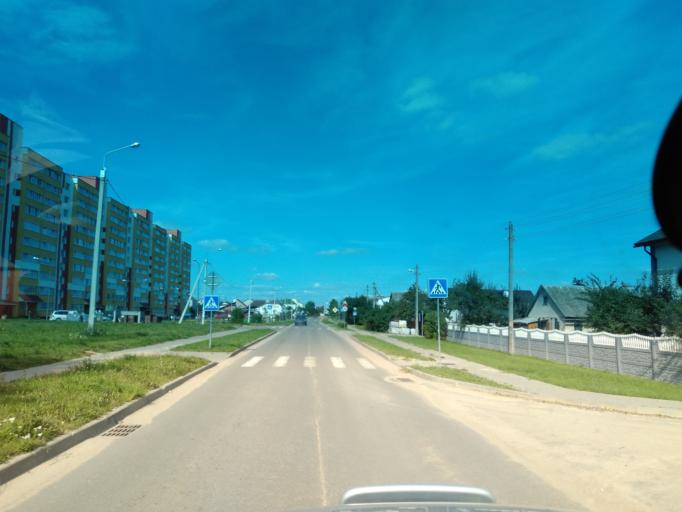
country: BY
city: Fanipol
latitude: 53.7508
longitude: 27.3350
